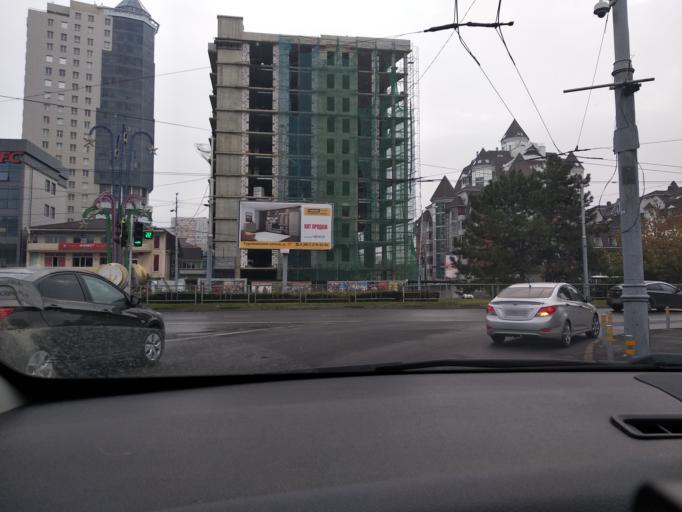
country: RU
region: Krasnodarskiy
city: Krasnodar
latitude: 45.0591
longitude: 38.9607
